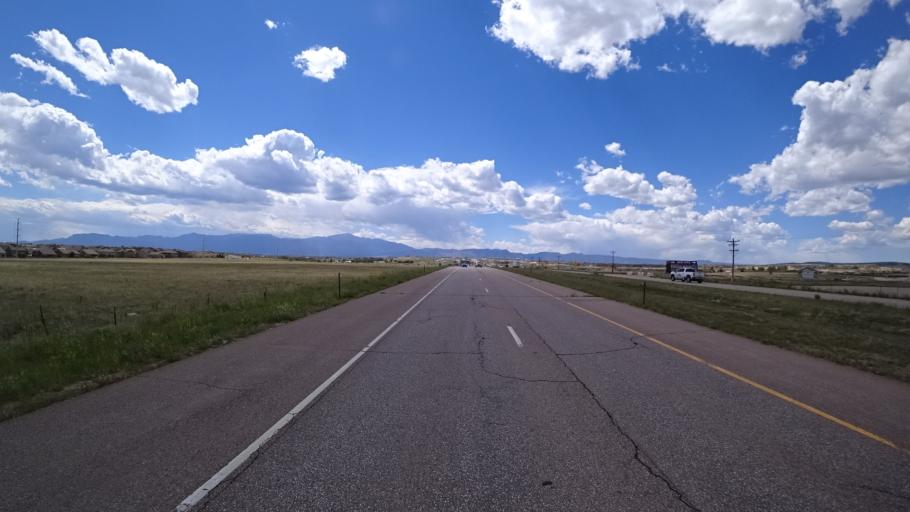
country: US
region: Colorado
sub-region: El Paso County
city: Black Forest
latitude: 38.9406
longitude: -104.6736
